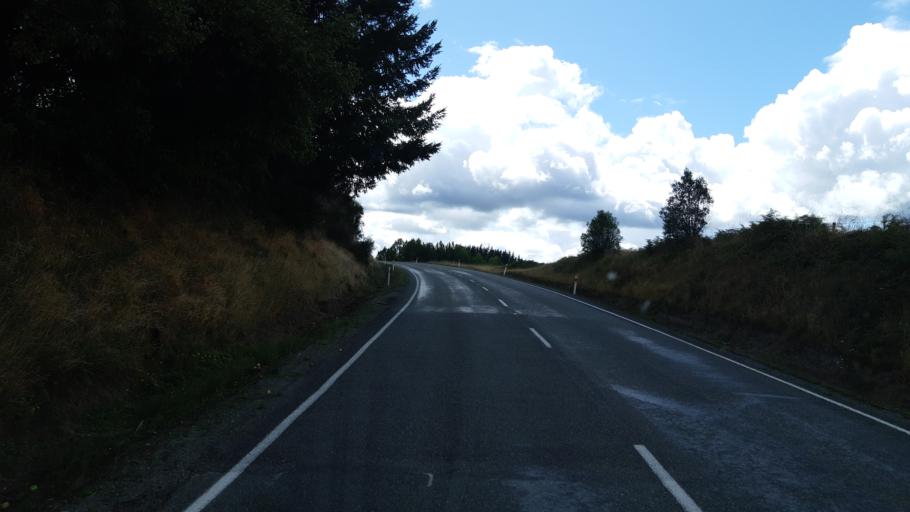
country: NZ
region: Tasman
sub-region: Tasman District
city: Wakefield
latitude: -41.5586
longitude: 172.7843
